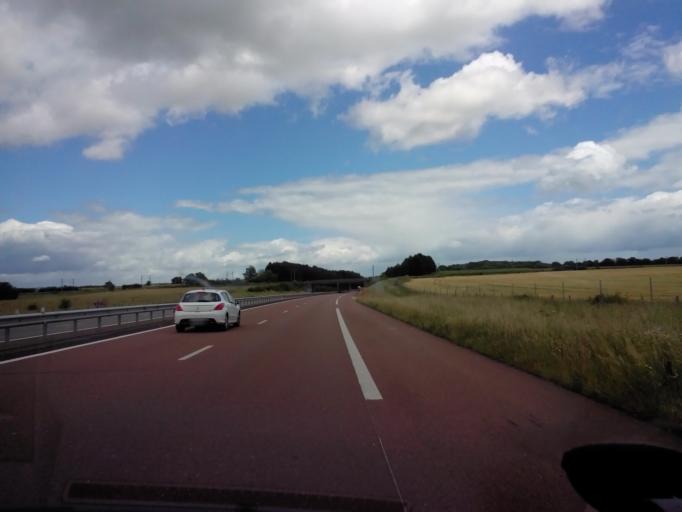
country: FR
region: Champagne-Ardenne
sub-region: Departement de la Haute-Marne
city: Saulxures
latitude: 48.0759
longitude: 5.6035
